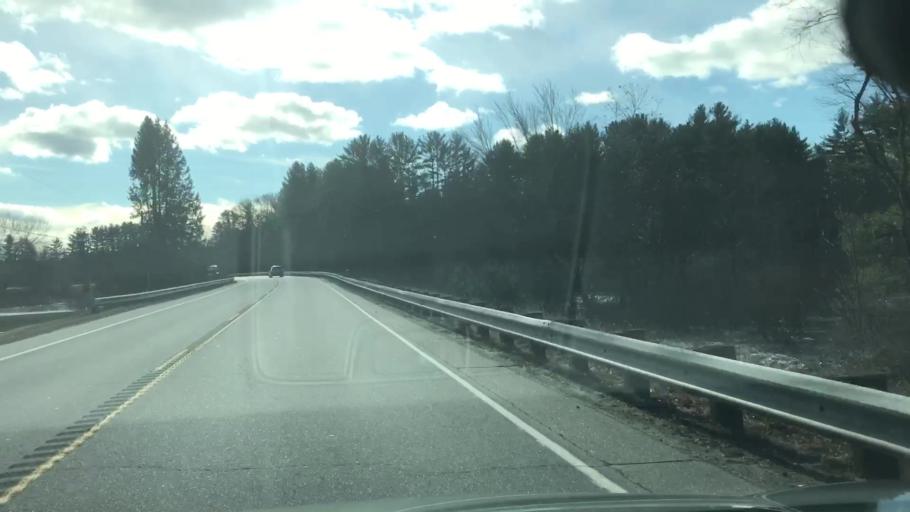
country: US
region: New Hampshire
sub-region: Merrimack County
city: Chichester
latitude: 43.2536
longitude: -71.3737
